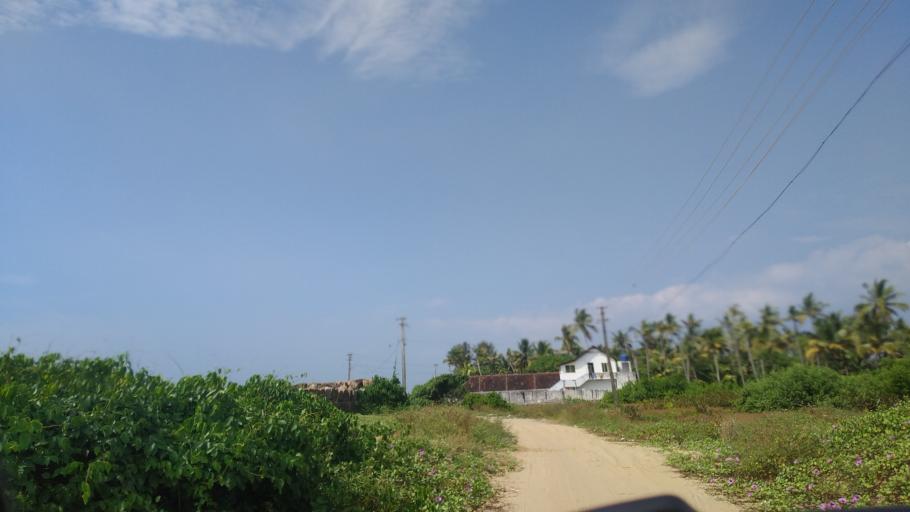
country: IN
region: Kerala
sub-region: Ernakulam
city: Elur
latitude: 10.0846
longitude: 76.1938
